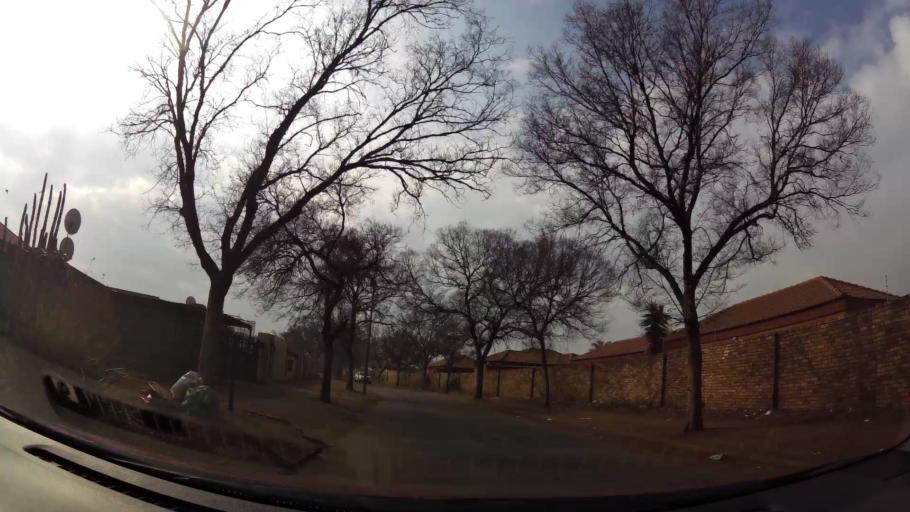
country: ZA
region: Gauteng
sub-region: Sedibeng District Municipality
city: Vanderbijlpark
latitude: -26.6908
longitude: 27.8391
